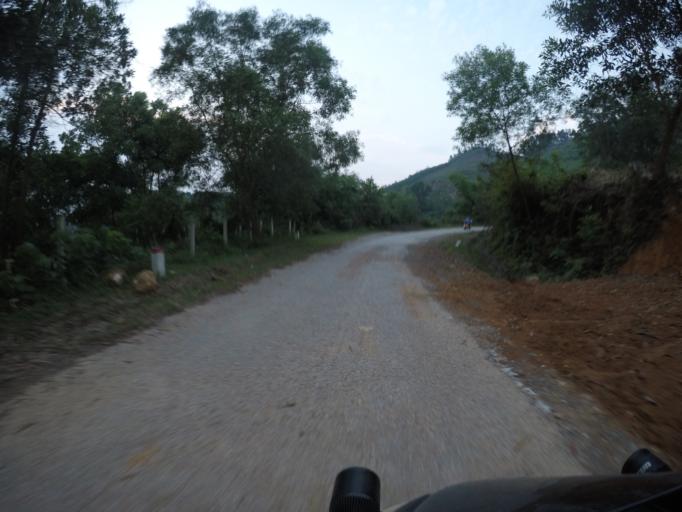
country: VN
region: Thai Nguyen
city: Chua Hang
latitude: 21.5824
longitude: 105.7121
